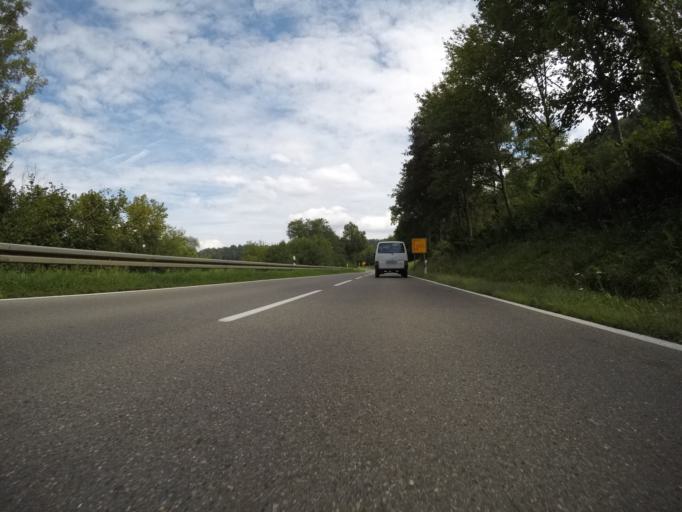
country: DE
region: Baden-Wuerttemberg
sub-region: Tuebingen Region
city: Hirrlingen
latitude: 48.4566
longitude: 8.8915
